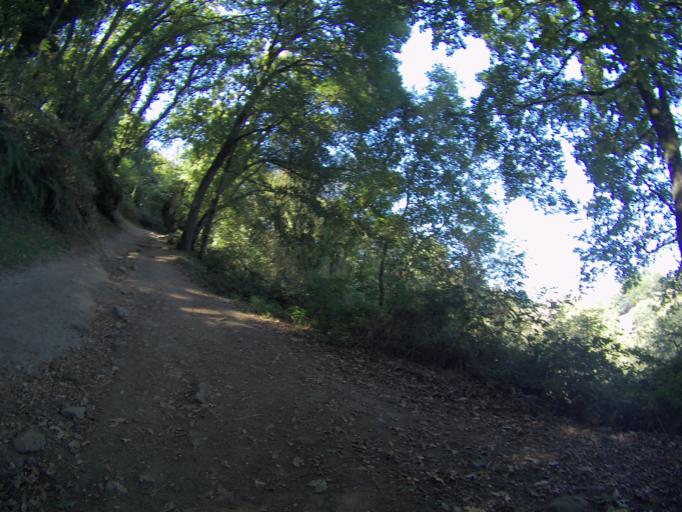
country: ES
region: Galicia
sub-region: Provincia de Lugo
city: Sarria
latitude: 42.7724
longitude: -7.4339
